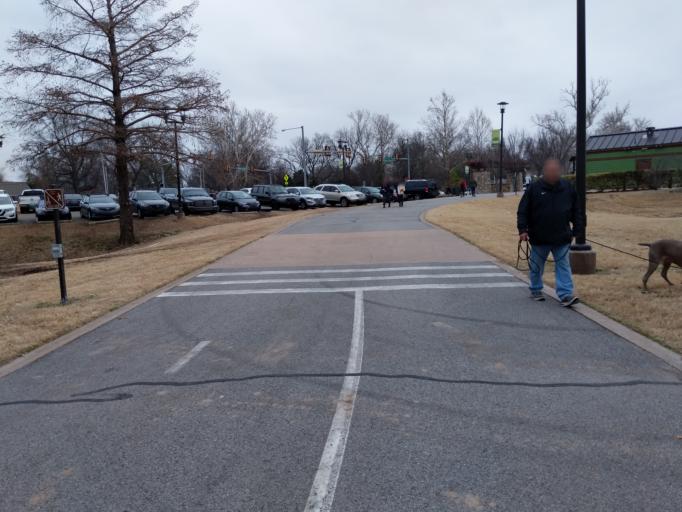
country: US
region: Oklahoma
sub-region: Tulsa County
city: Tulsa
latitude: 36.1050
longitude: -95.9842
